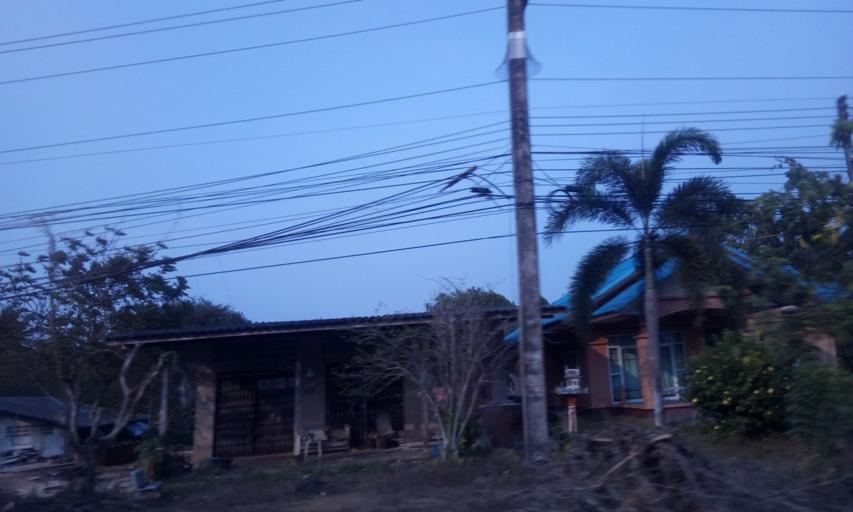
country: TH
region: Chanthaburi
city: Khlung
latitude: 12.4119
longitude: 102.3313
